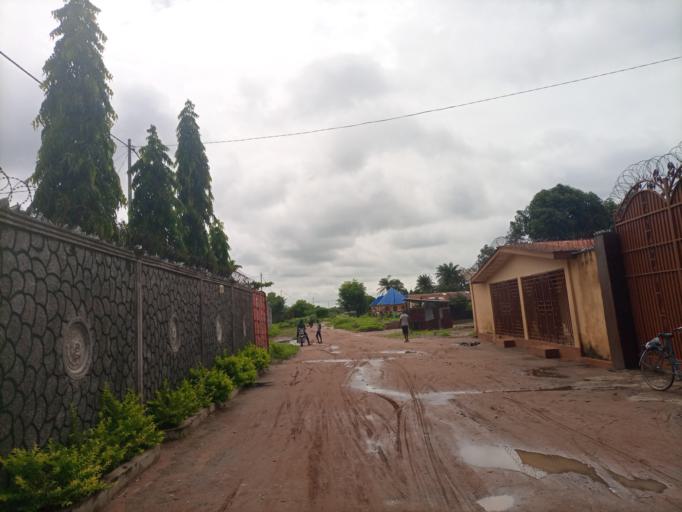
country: SL
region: Northern Province
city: Sawkta
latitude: 8.6243
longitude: -13.2000
